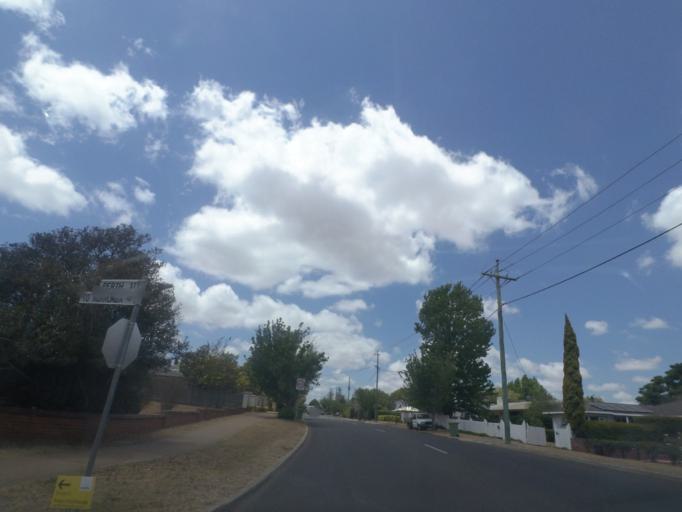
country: AU
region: Queensland
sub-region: Toowoomba
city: Rangeville
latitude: -27.5763
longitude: 151.9787
